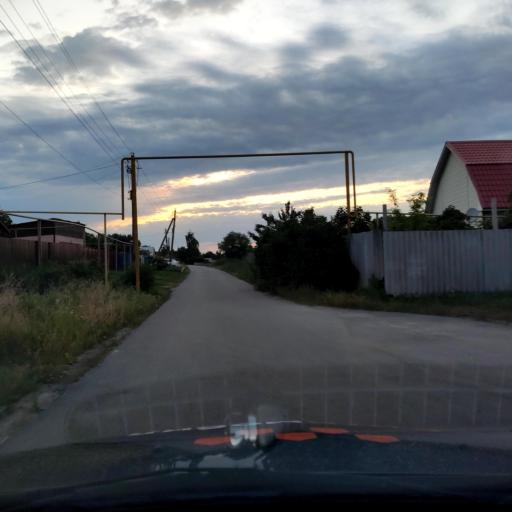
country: RU
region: Voronezj
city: Shilovo
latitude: 51.4531
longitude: 39.0305
